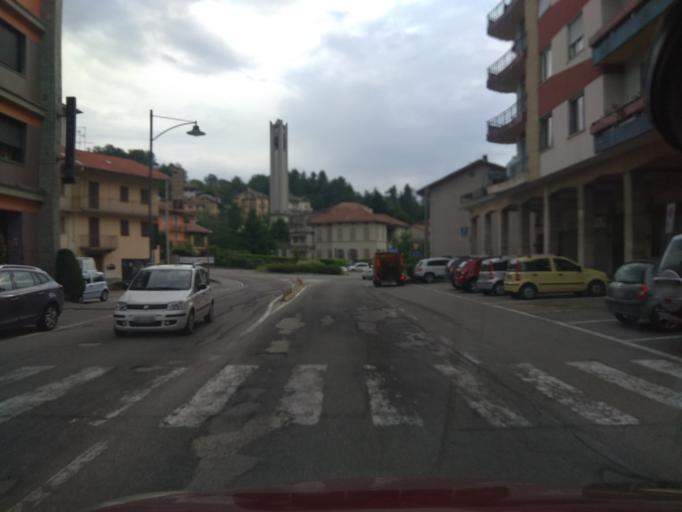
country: IT
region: Piedmont
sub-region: Provincia di Biella
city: Trivero-Prativero-Ponzone
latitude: 45.6548
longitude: 8.1880
